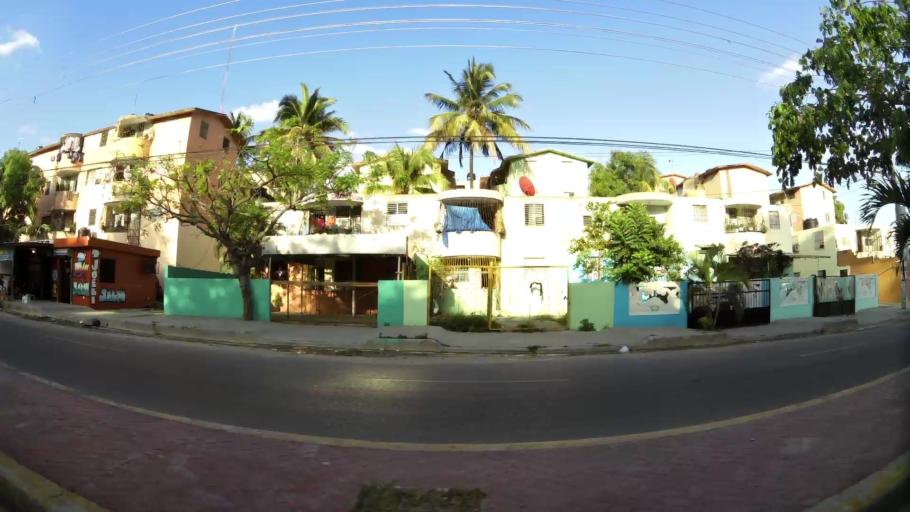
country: DO
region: Nacional
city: La Agustina
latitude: 18.5415
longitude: -69.9276
